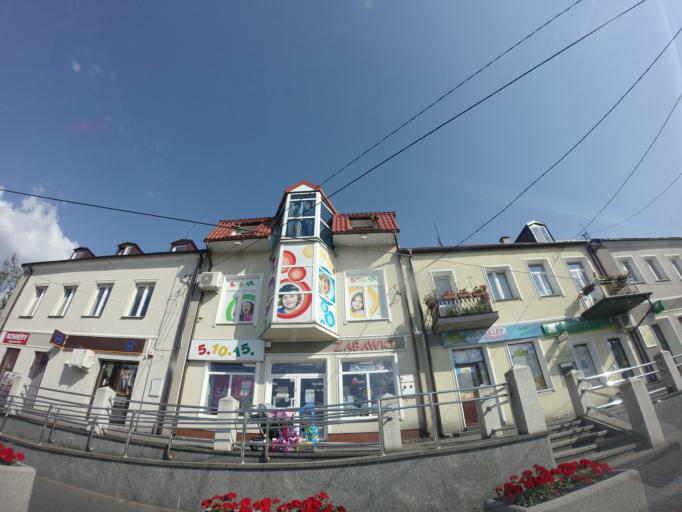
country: PL
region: Masovian Voivodeship
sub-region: Powiat sokolowski
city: Sokolow Podlaski
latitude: 52.4056
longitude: 22.2549
